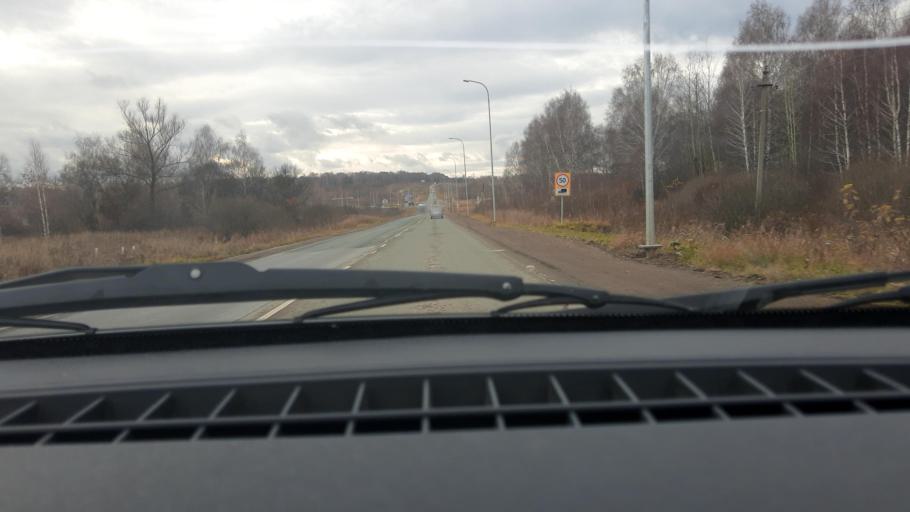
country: RU
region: Bashkortostan
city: Iglino
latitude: 54.8172
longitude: 56.3700
